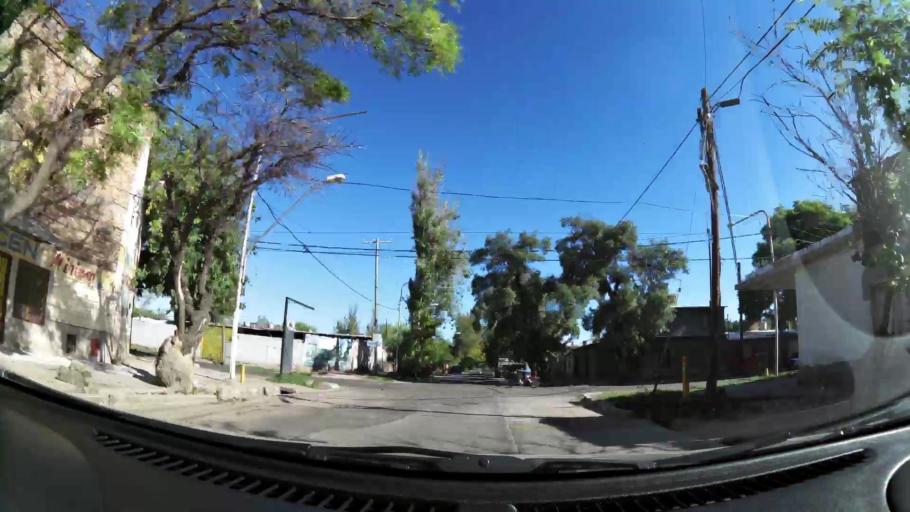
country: AR
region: Mendoza
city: Las Heras
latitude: -32.8518
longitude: -68.8311
